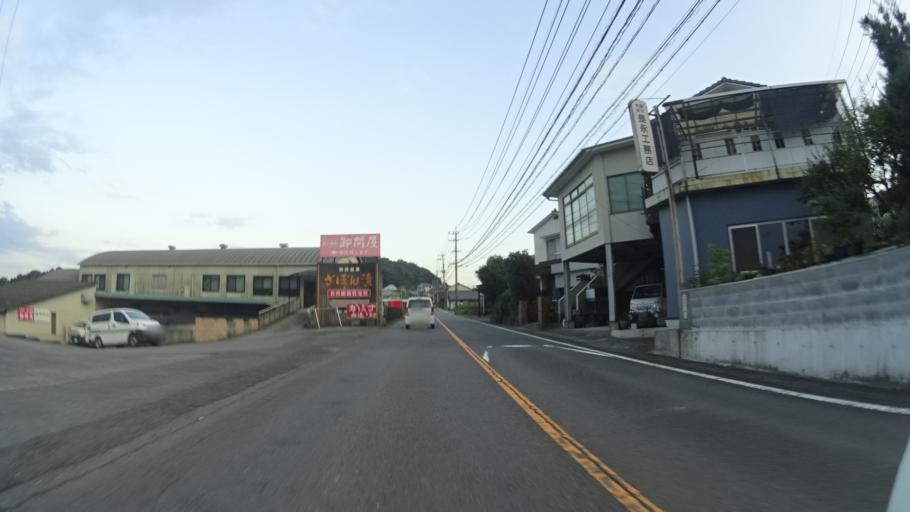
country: JP
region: Oita
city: Beppu
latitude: 33.3220
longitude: 131.4791
